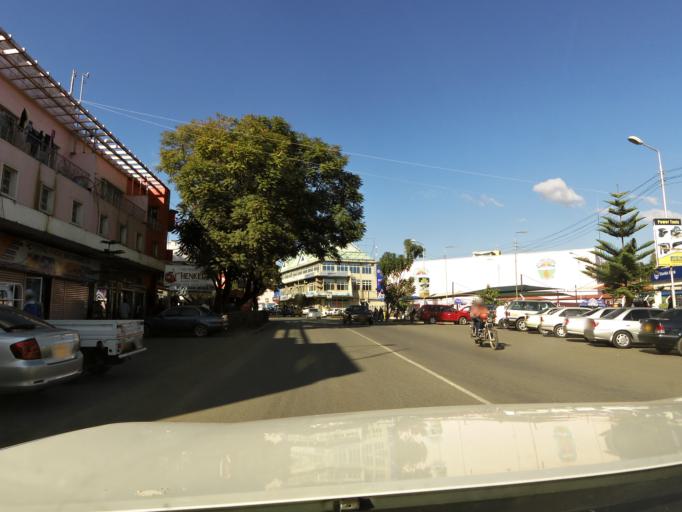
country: TZ
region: Arusha
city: Arusha
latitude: -3.3733
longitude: 36.6922
